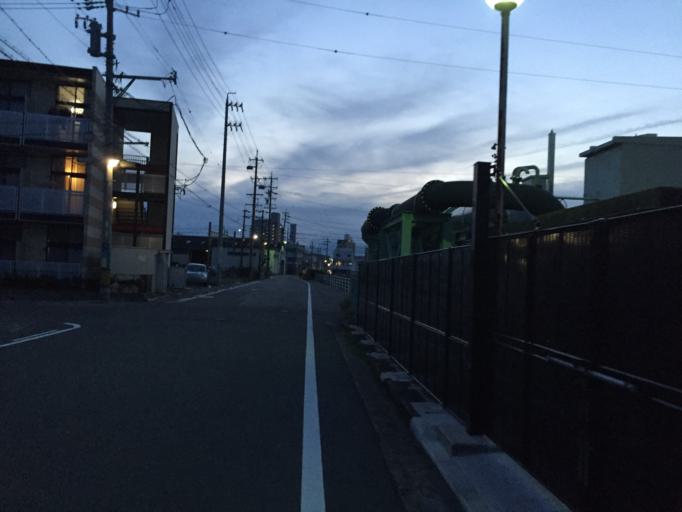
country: JP
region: Mie
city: Yokkaichi
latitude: 34.9588
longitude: 136.6295
